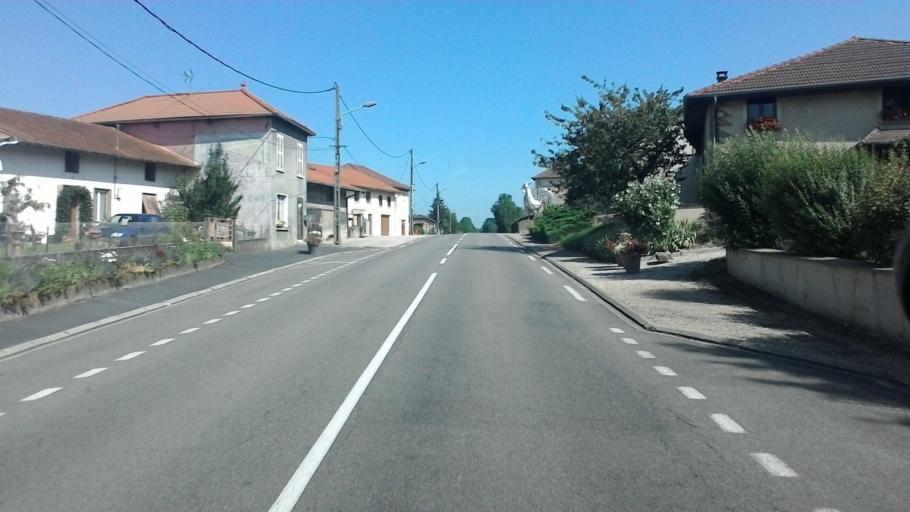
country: FR
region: Rhone-Alpes
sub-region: Departement de l'Ain
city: Saint-Trivier-de-Courtes
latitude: 46.4244
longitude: 5.0988
